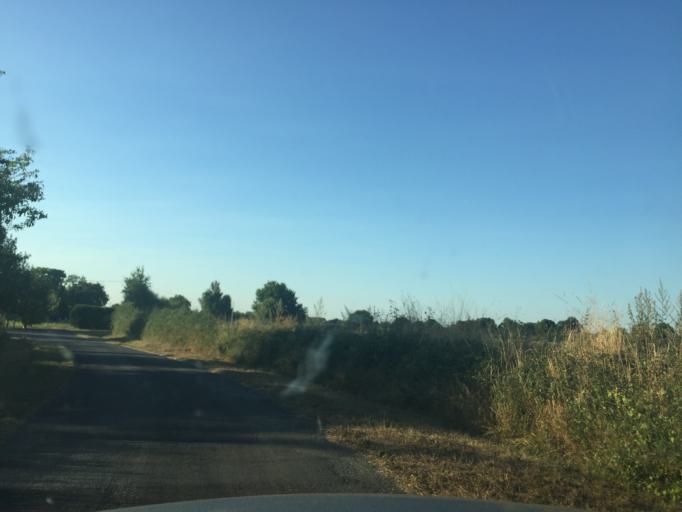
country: FR
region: Poitou-Charentes
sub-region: Departement des Deux-Sevres
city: Lezay
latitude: 46.2008
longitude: -0.0367
